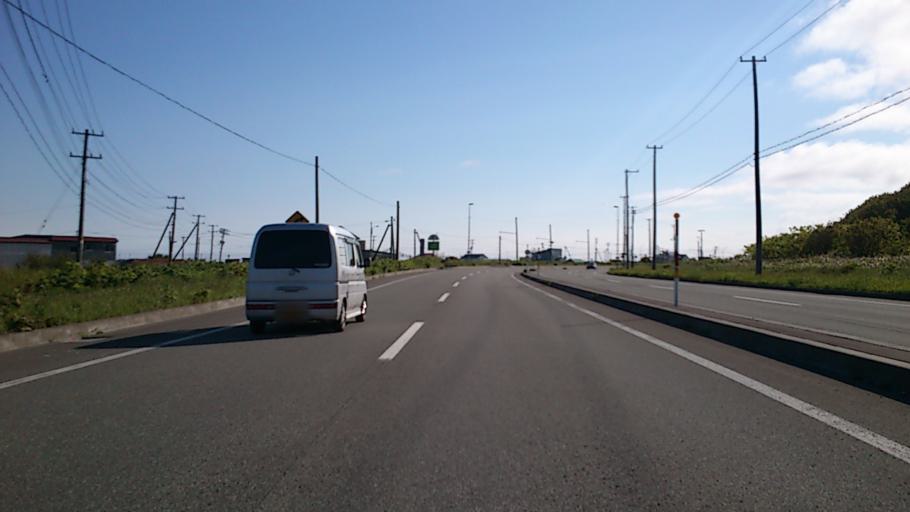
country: JP
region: Hokkaido
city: Wakkanai
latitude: 45.4032
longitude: 141.7456
